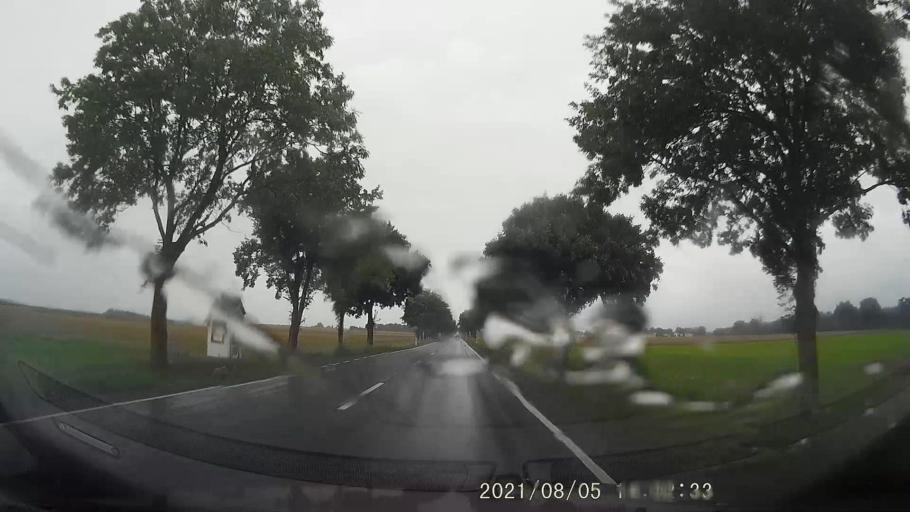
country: PL
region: Opole Voivodeship
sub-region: Powiat krapkowicki
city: Strzeleczki
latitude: 50.4559
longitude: 17.8731
